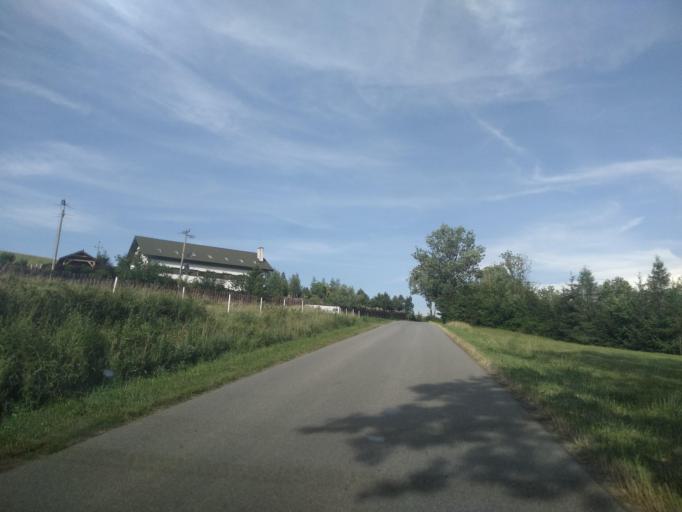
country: PL
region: Subcarpathian Voivodeship
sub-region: Powiat sanocki
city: Rzepedz
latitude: 49.4293
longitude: 22.1299
